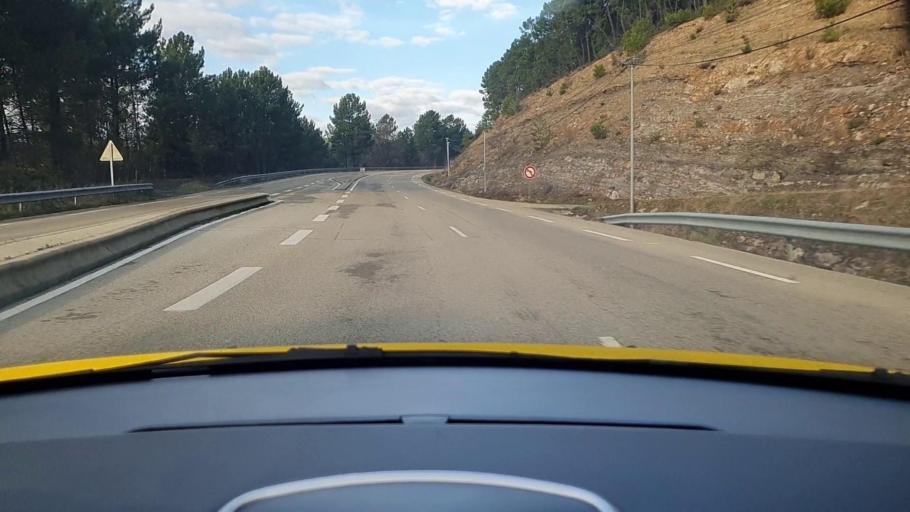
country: FR
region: Languedoc-Roussillon
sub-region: Departement du Gard
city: Les Salles-du-Gardon
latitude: 44.2591
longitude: 4.0399
